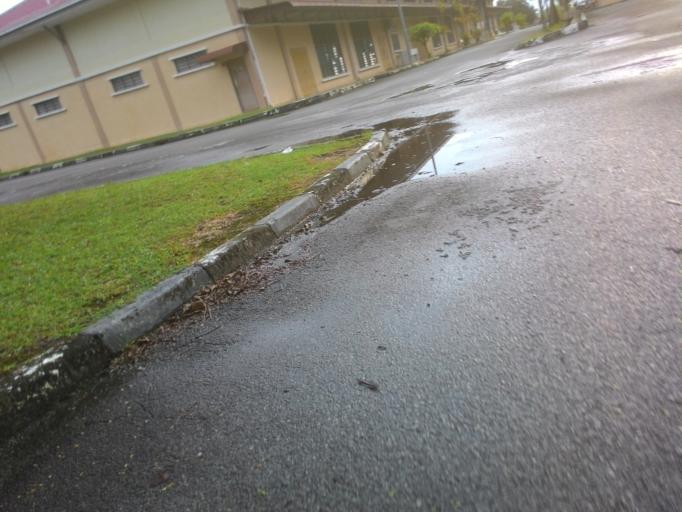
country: MY
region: Kedah
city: Kulim
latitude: 5.3854
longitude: 100.5777
